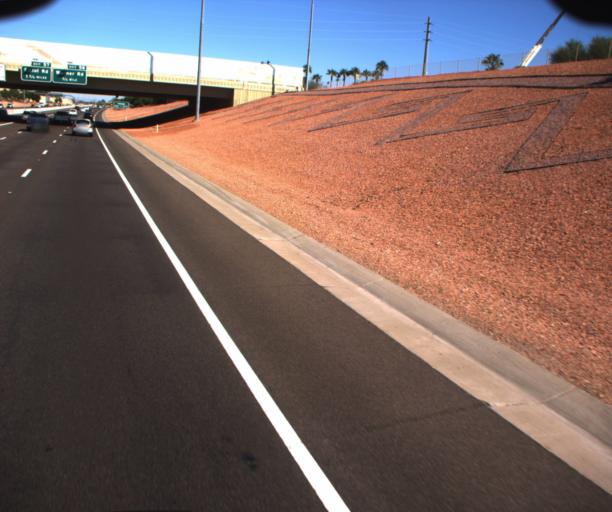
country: US
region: Arizona
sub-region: Maricopa County
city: San Carlos
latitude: 33.3193
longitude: -111.8941
